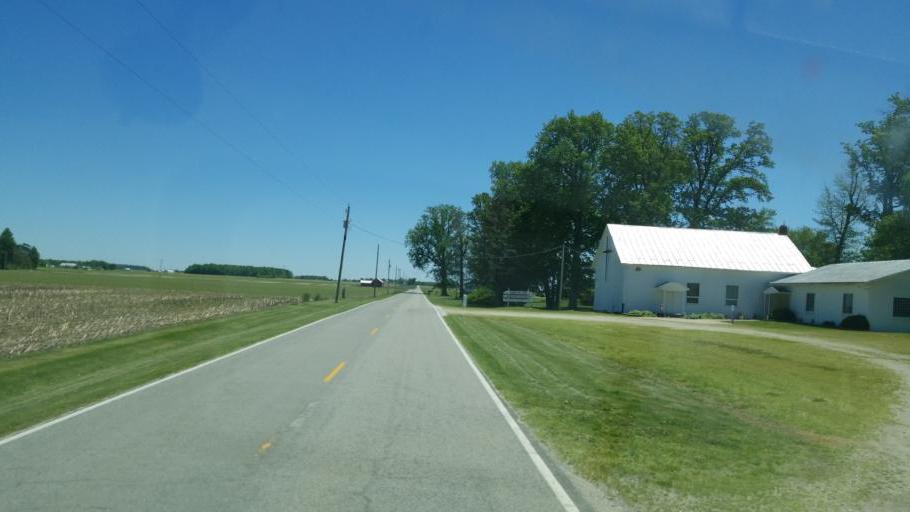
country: US
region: Ohio
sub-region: Darke County
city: Union City
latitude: 40.2815
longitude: -84.7522
